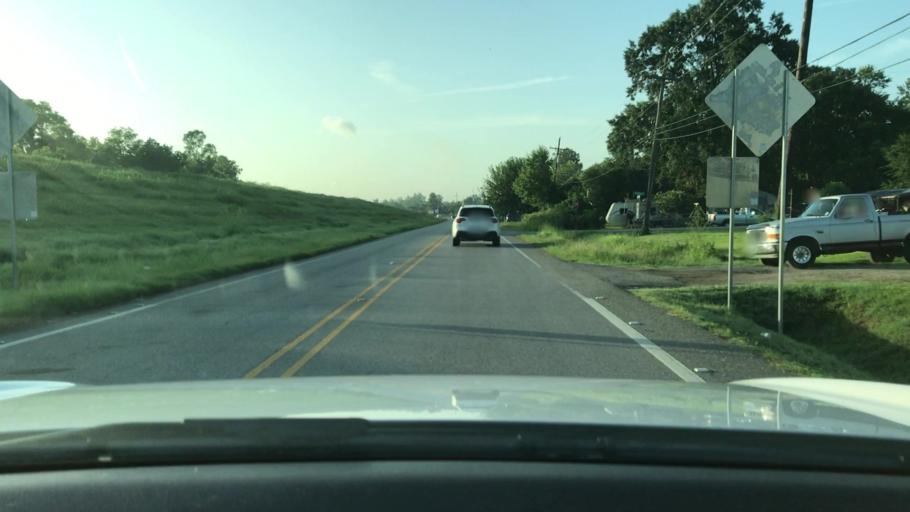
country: US
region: Louisiana
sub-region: Iberville Parish
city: Plaquemine
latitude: 30.2828
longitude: -91.2246
